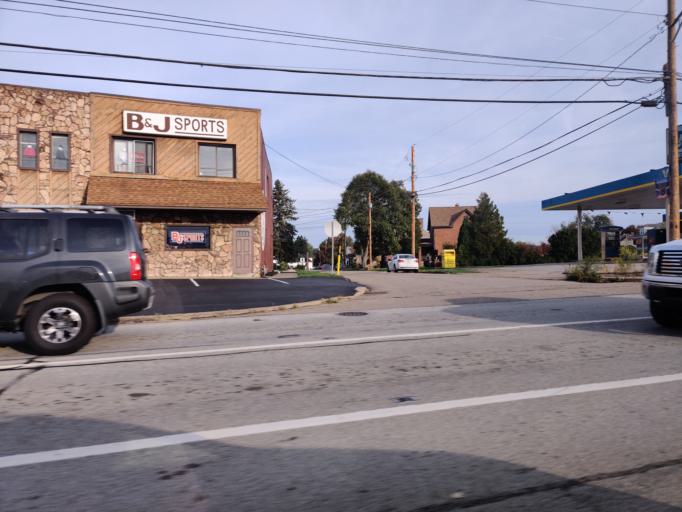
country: US
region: Pennsylvania
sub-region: Allegheny County
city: Brackenridge
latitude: 40.6212
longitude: -79.7284
